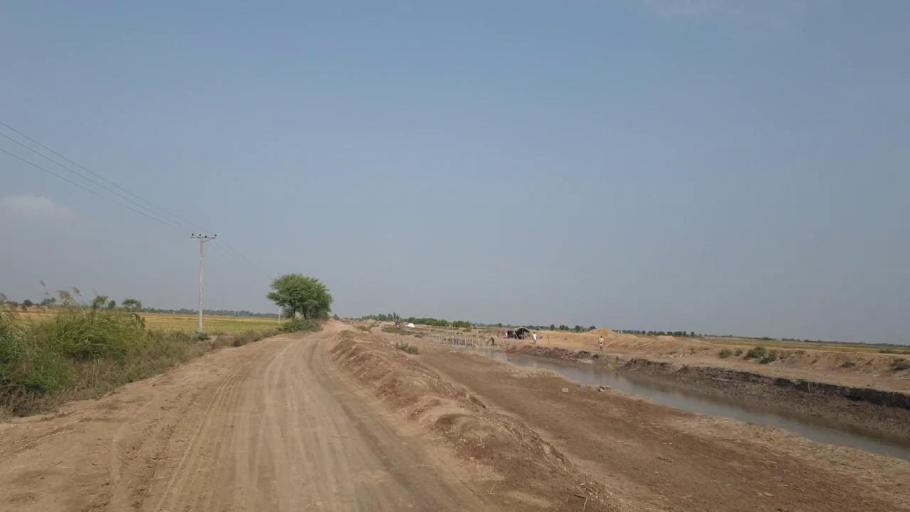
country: PK
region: Sindh
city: Badin
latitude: 24.7407
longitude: 68.7648
